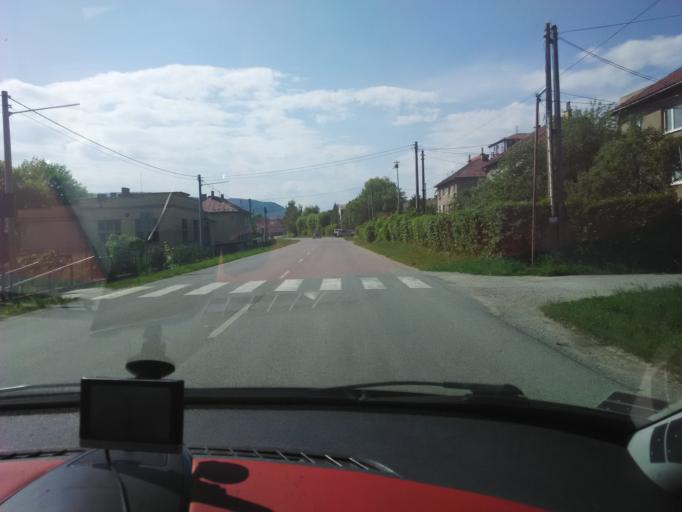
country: SK
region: Banskobystricky
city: Revuca
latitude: 48.6254
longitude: 20.2448
